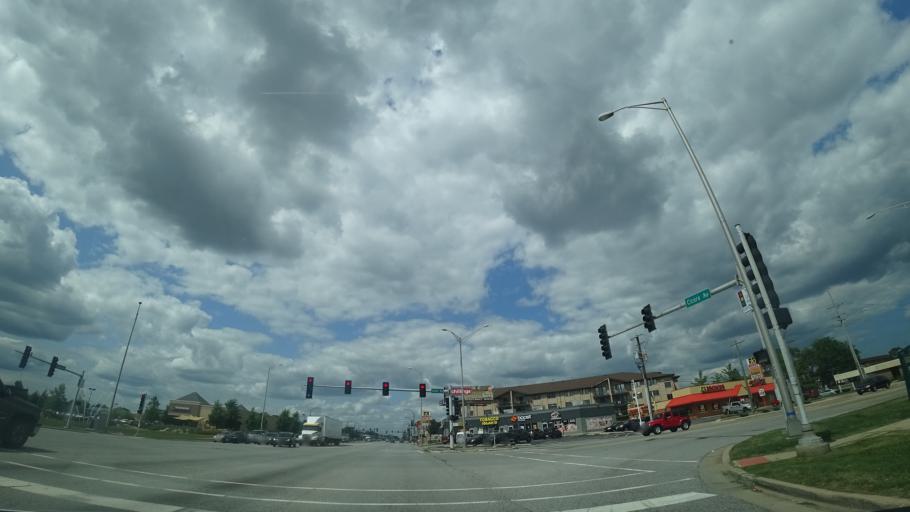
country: US
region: Illinois
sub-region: Cook County
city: Alsip
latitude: 41.6907
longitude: -87.7397
